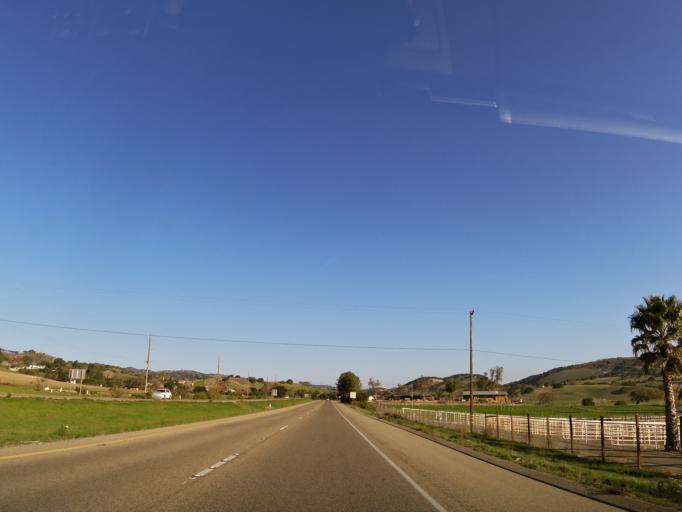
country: US
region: California
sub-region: Santa Barbara County
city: Buellton
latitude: 34.6276
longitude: -120.1882
